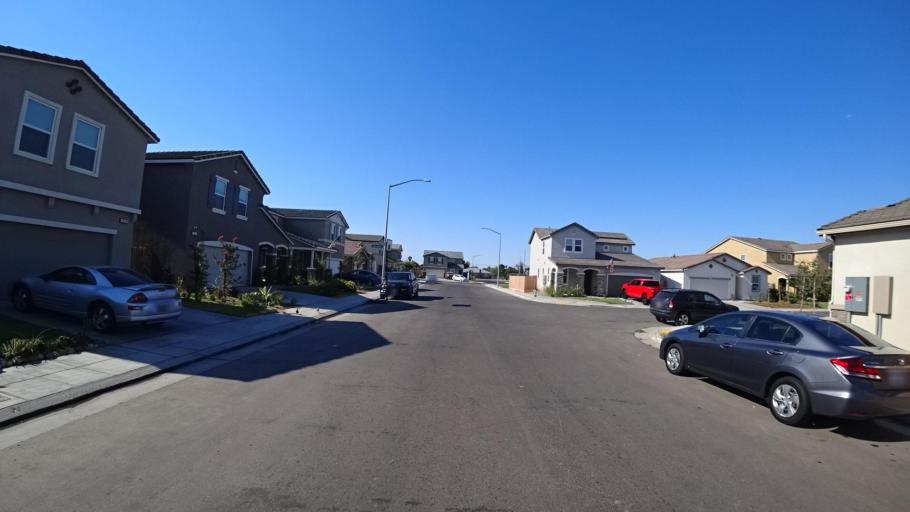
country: US
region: California
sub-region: Fresno County
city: Sunnyside
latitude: 36.7156
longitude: -119.7310
